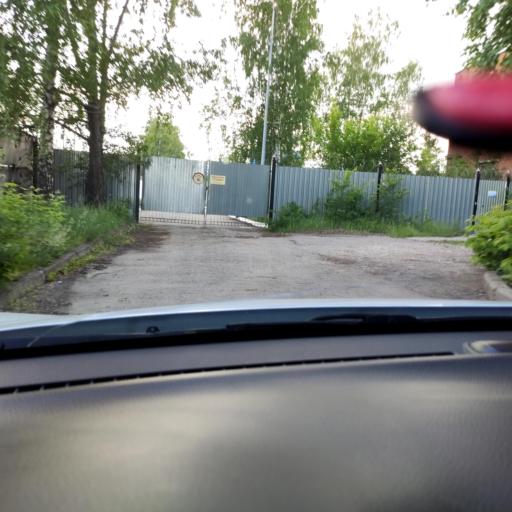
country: RU
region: Tatarstan
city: Staroye Arakchino
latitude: 55.8282
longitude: 49.0365
